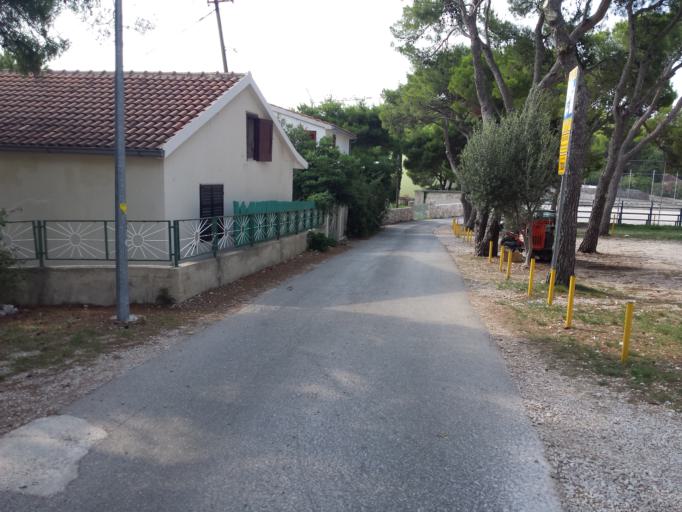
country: HR
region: Sibensko-Kniniska
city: Rogoznica
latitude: 43.5263
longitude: 15.9713
